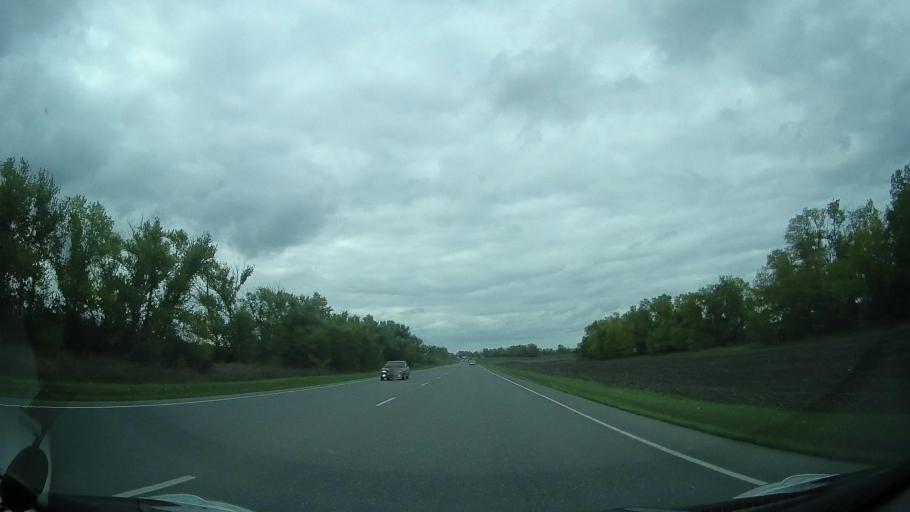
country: RU
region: Rostov
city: Mechetinskaya
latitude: 46.7465
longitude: 40.4653
